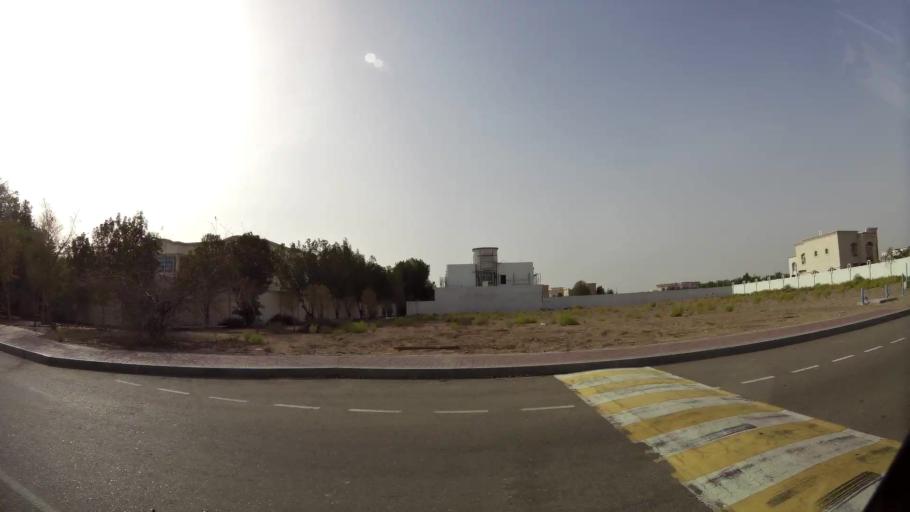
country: AE
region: Abu Dhabi
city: Al Ain
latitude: 24.2014
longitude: 55.6296
